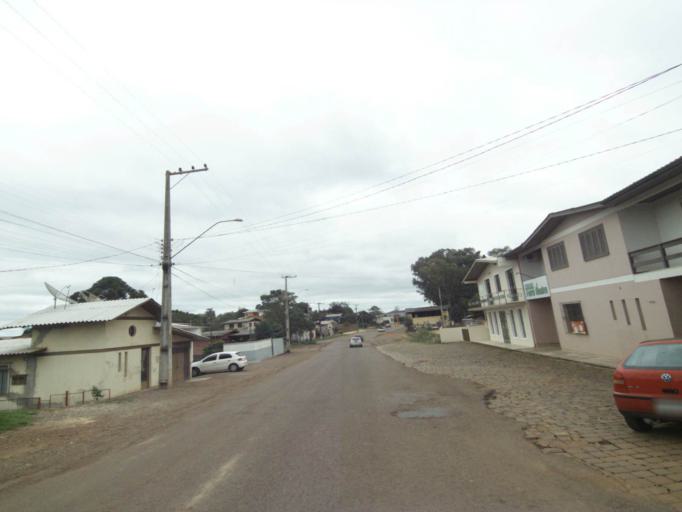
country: BR
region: Rio Grande do Sul
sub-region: Lagoa Vermelha
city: Lagoa Vermelha
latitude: -28.2126
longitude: -51.5278
